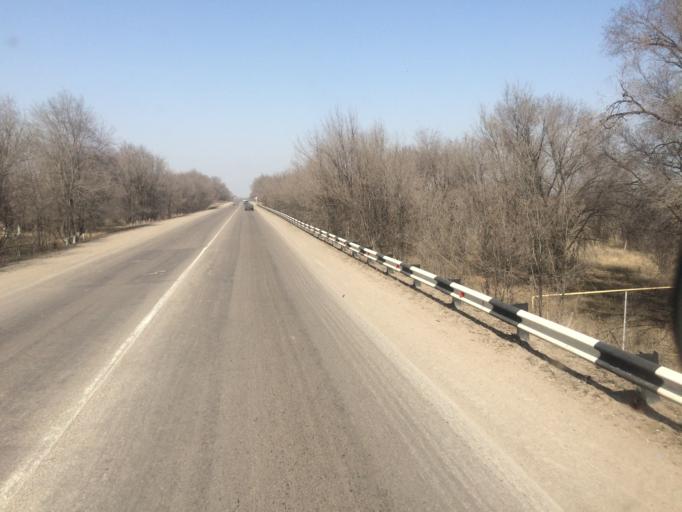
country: KZ
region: Almaty Oblysy
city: Burunday
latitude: 43.3122
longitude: 76.6656
